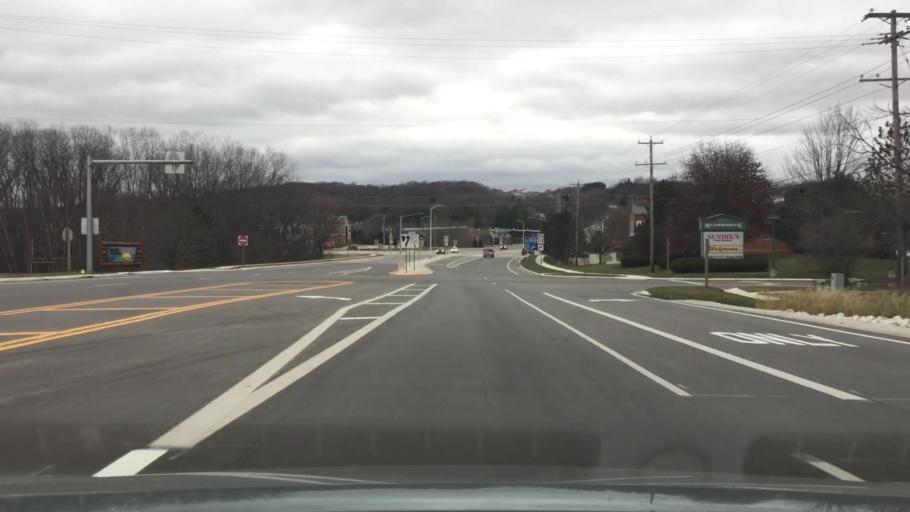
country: US
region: Wisconsin
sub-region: Waukesha County
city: Waukesha
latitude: 43.0206
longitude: -88.2829
